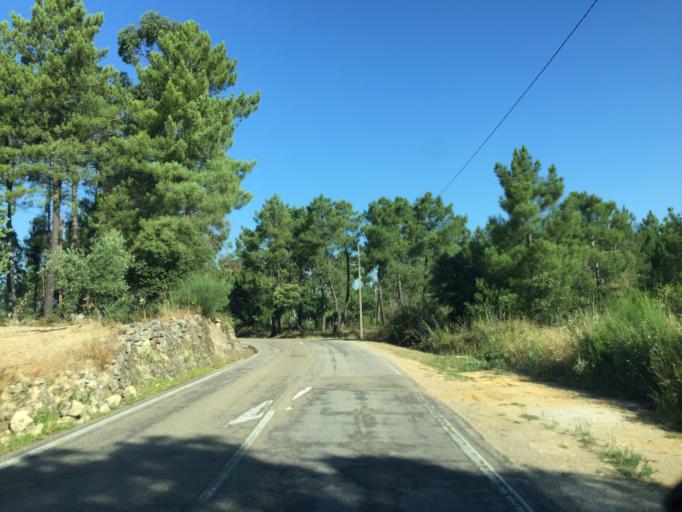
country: PT
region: Santarem
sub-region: Abrantes
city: Alferrarede
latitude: 39.5331
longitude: -8.1376
